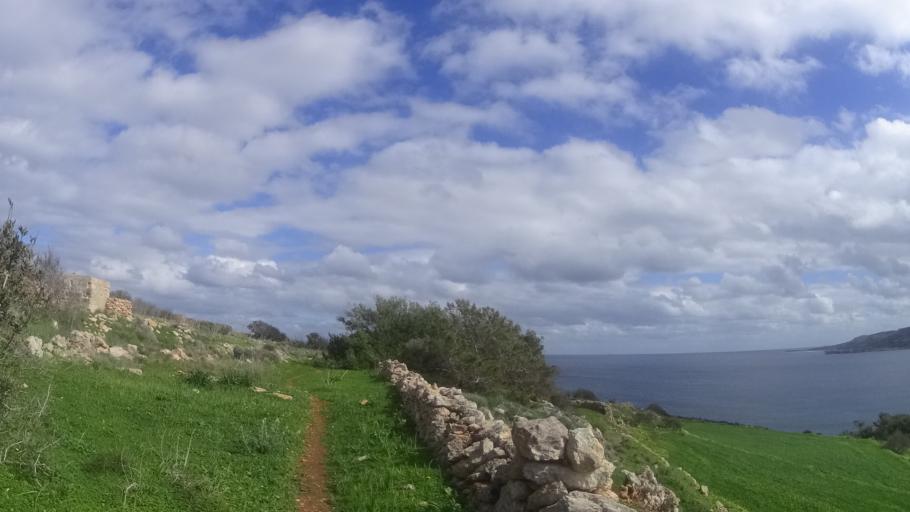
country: MT
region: Il-Mellieha
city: Mellieha
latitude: 35.9782
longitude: 14.3552
